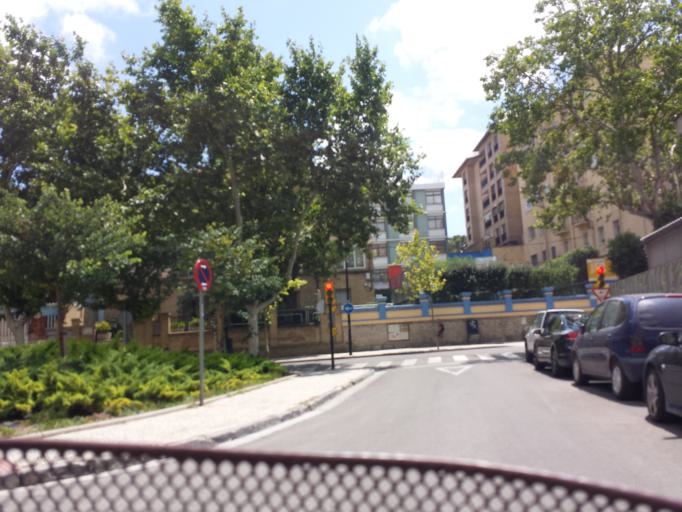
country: ES
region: Aragon
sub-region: Provincia de Zaragoza
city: Zaragoza
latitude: 41.6384
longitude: -0.8871
